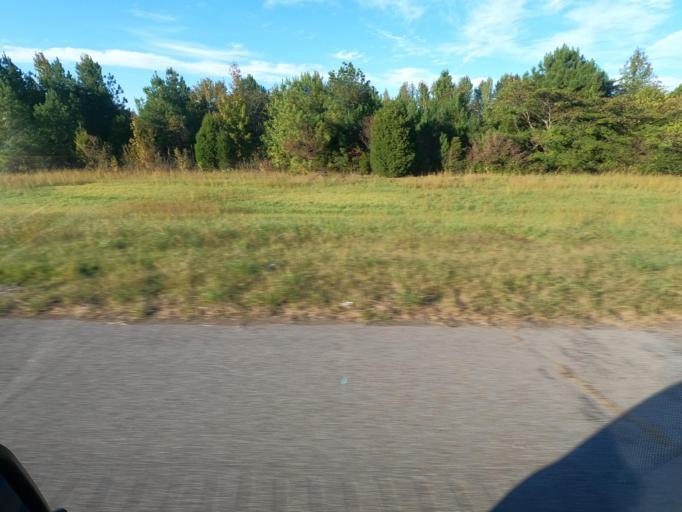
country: US
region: Tennessee
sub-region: Shelby County
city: Lakeland
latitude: 35.3079
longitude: -89.8034
